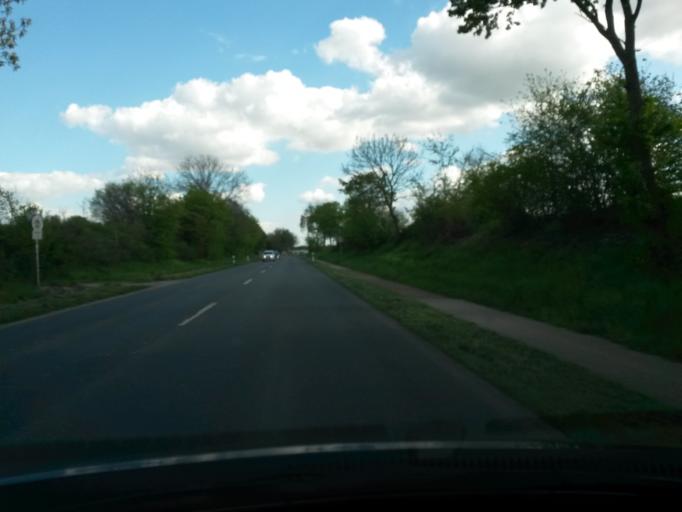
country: DE
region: North Rhine-Westphalia
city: Wegberg
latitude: 51.1638
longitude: 6.3469
